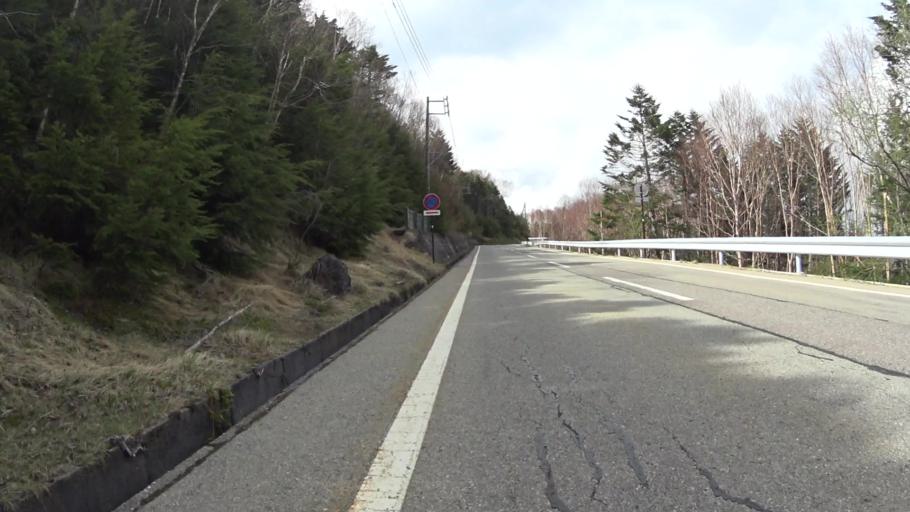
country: JP
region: Nagano
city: Saku
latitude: 36.0557
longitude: 138.3544
